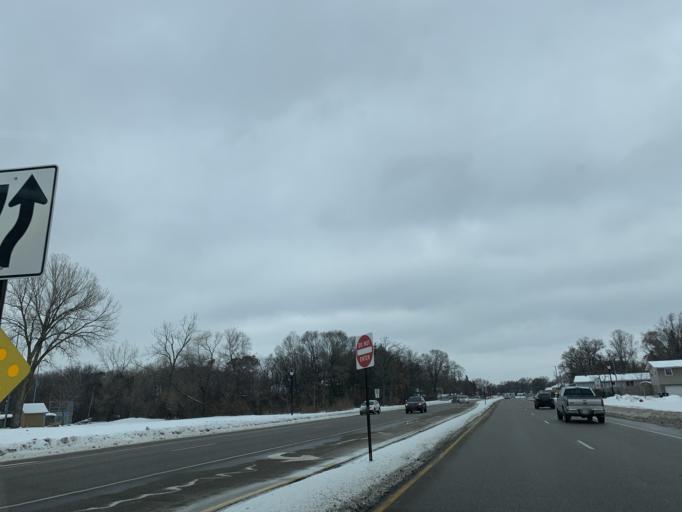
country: US
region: Minnesota
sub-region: Anoka County
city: Blaine
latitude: 45.1572
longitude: -93.2737
